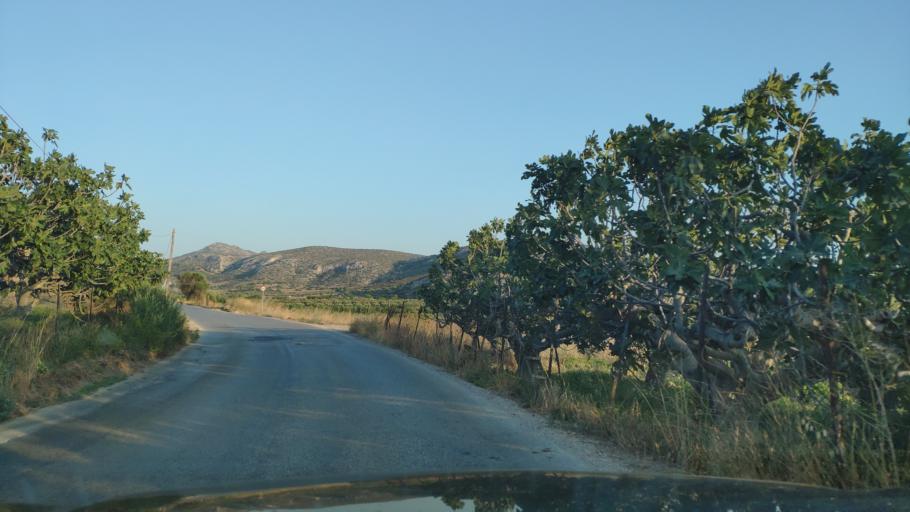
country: GR
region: Attica
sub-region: Nomarchia Anatolikis Attikis
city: Artemida
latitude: 37.9284
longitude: 23.9816
